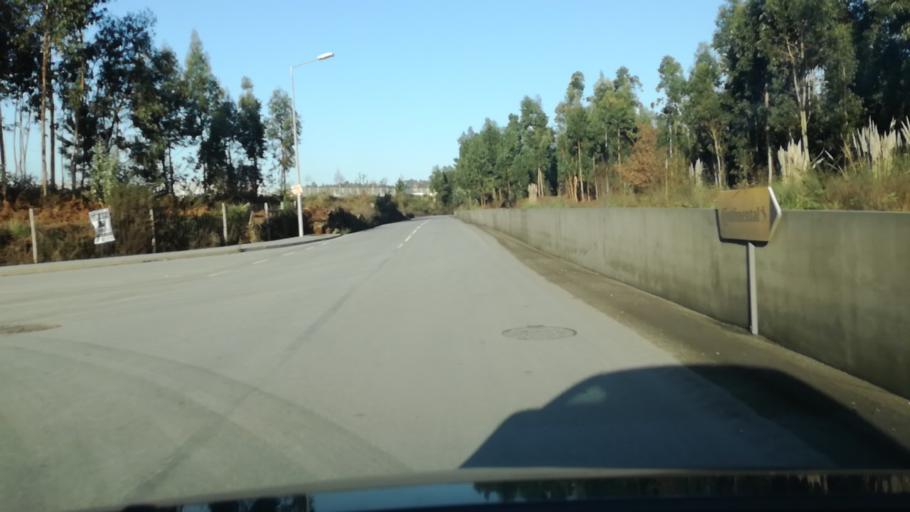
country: PT
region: Braga
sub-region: Vila Nova de Famalicao
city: Ferreiros
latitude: 41.3636
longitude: -8.5359
